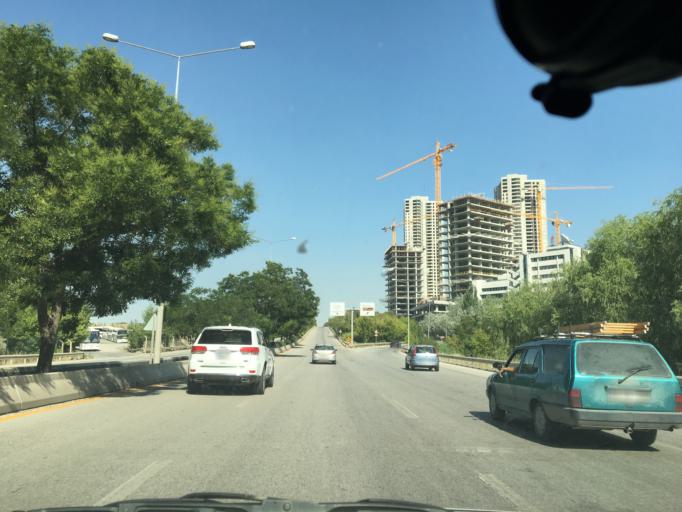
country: TR
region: Ankara
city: Ankara
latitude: 39.9184
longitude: 32.7849
